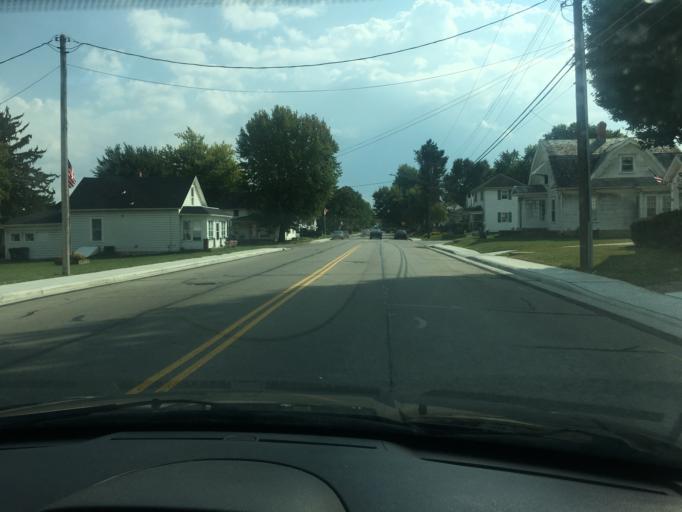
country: US
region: Ohio
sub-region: Champaign County
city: Urbana
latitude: 40.1155
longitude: -83.7645
